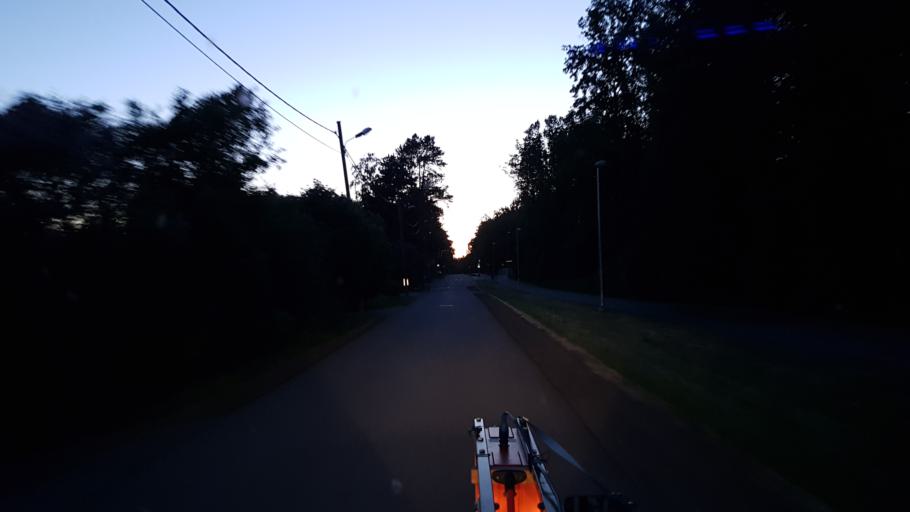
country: EE
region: Harju
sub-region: Harku vald
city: Tabasalu
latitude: 59.4546
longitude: 24.5795
